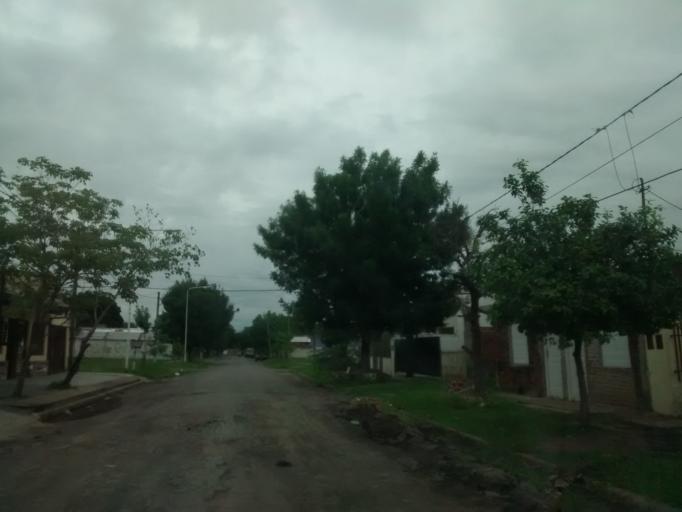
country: AR
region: Chaco
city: Puerto Tirol
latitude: -27.3709
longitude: -59.0960
